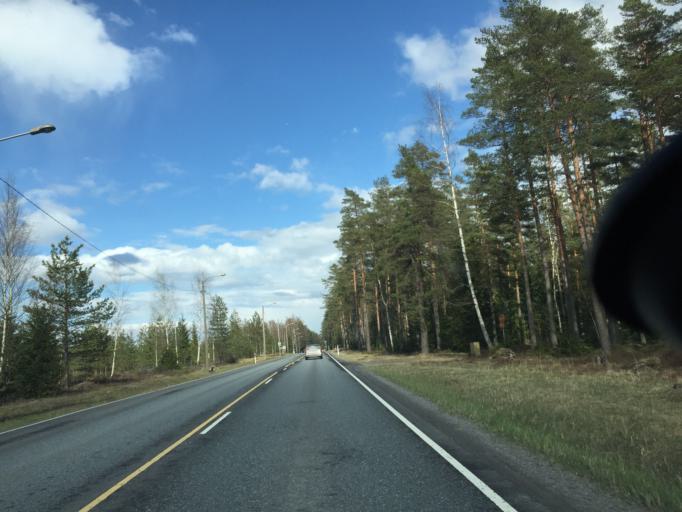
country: FI
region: Uusimaa
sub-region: Raaseporin
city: Karis
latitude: 60.1088
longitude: 23.7889
